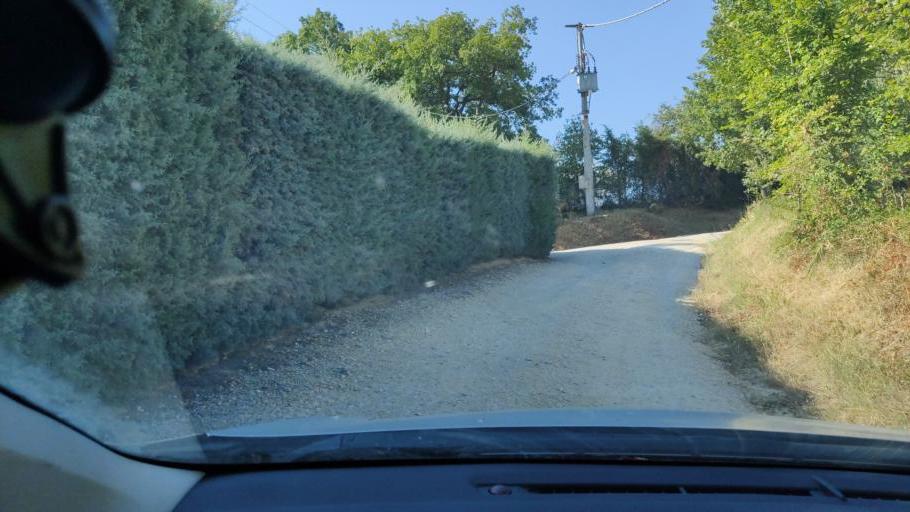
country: IT
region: Umbria
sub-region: Provincia di Terni
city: Fornole
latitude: 42.5193
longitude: 12.4332
